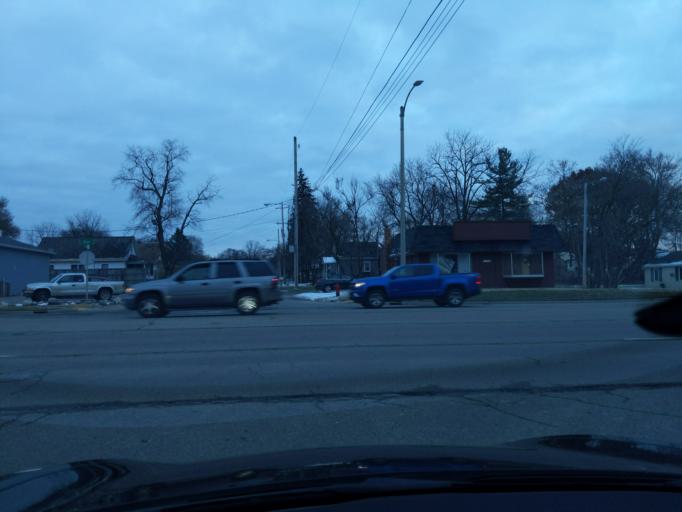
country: US
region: Michigan
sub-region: Ingham County
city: Lansing
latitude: 42.7656
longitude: -84.5429
